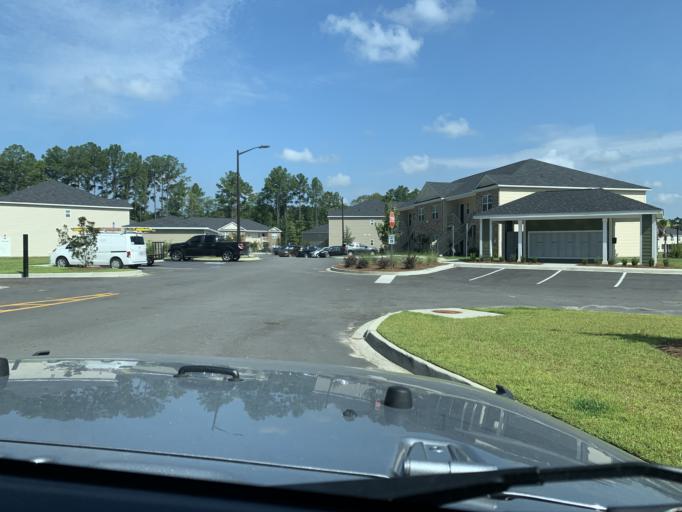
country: US
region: Georgia
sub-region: Chatham County
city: Bloomingdale
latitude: 32.1315
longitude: -81.2908
